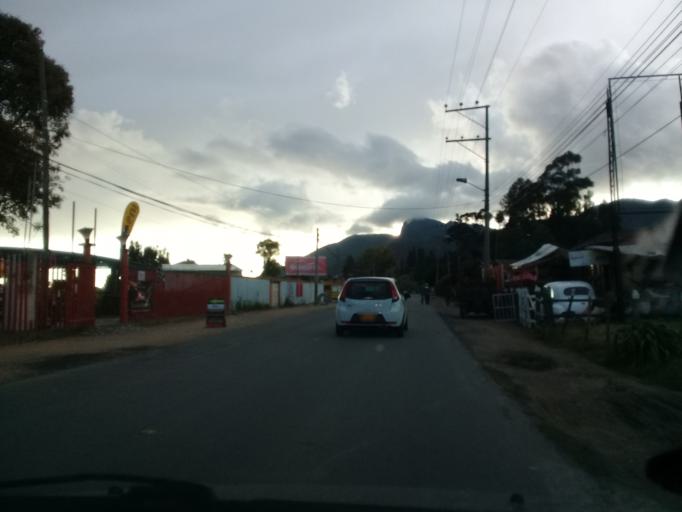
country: CO
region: Cundinamarca
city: Tabio
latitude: 4.9226
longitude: -74.0847
